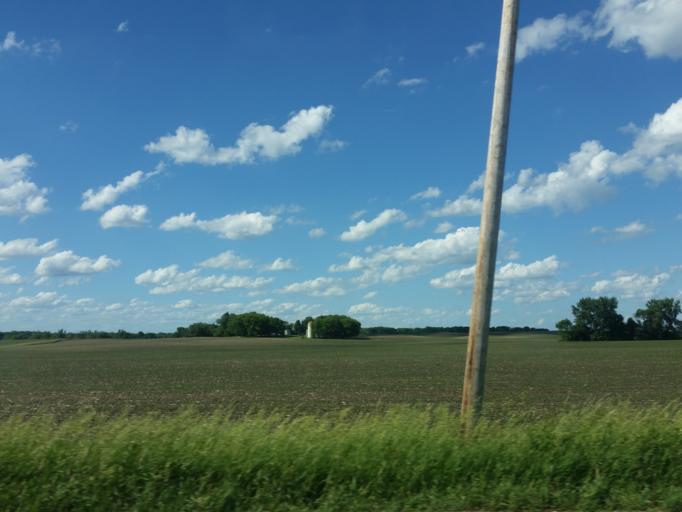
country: US
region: Minnesota
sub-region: Wright County
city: Cokato
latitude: 45.0661
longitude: -94.2384
